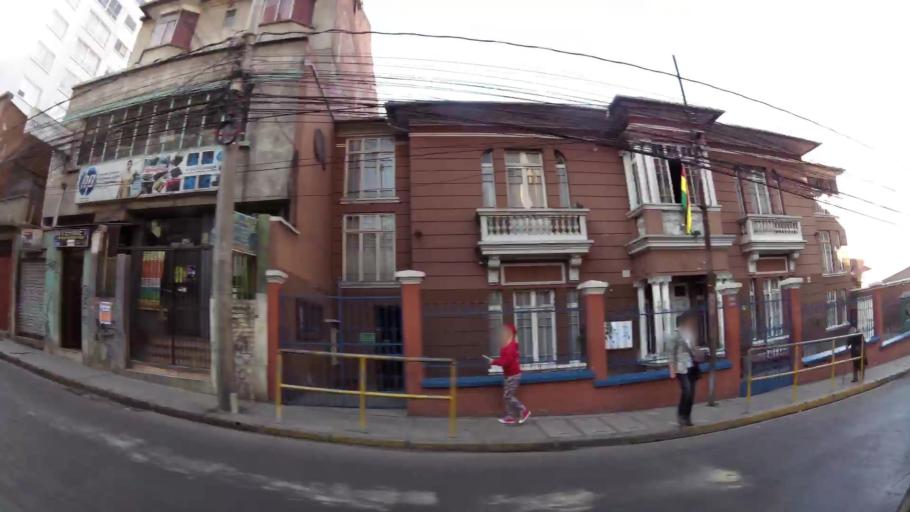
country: BO
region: La Paz
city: La Paz
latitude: -16.5038
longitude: -68.1291
